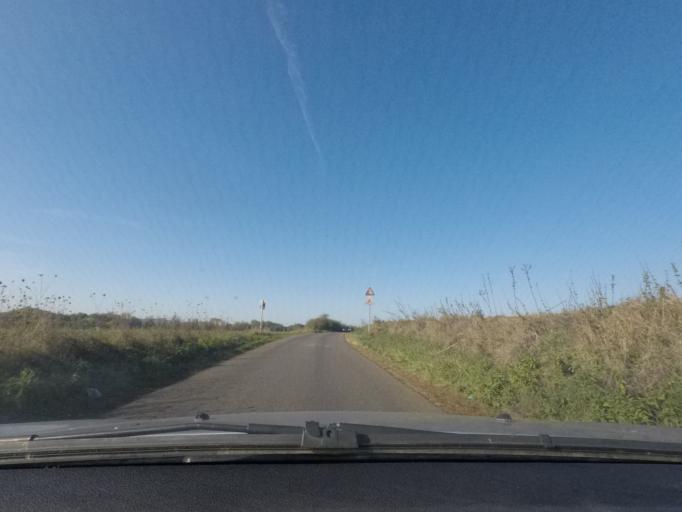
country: BE
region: Wallonia
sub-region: Province du Luxembourg
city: Arlon
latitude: 49.6438
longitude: 5.7861
